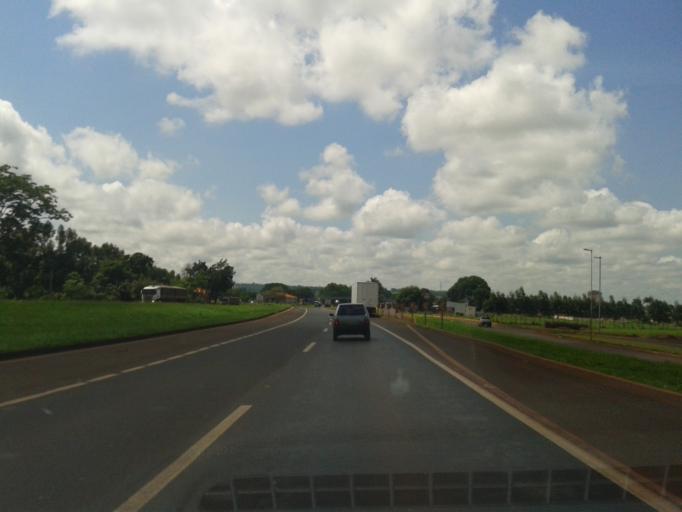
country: BR
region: Minas Gerais
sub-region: Centralina
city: Centralina
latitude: -18.5762
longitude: -49.1938
